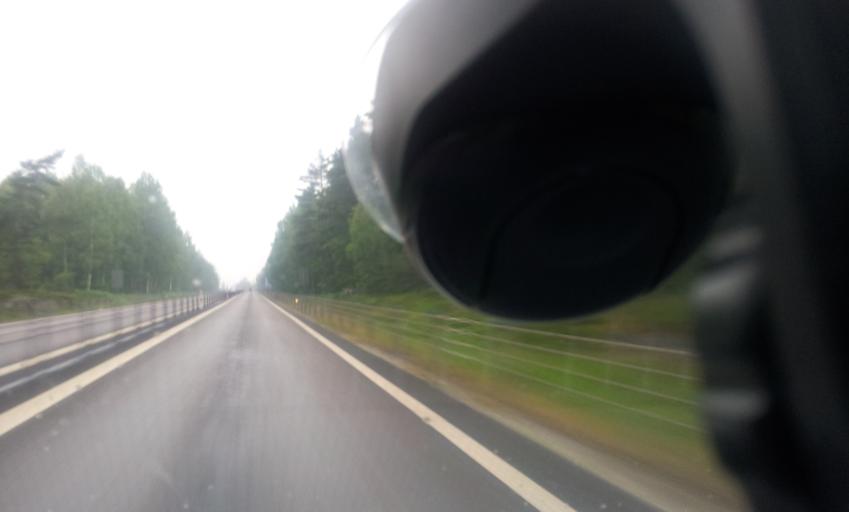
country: SE
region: Kalmar
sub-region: Vasterviks Kommun
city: Gamleby
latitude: 57.8135
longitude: 16.4866
